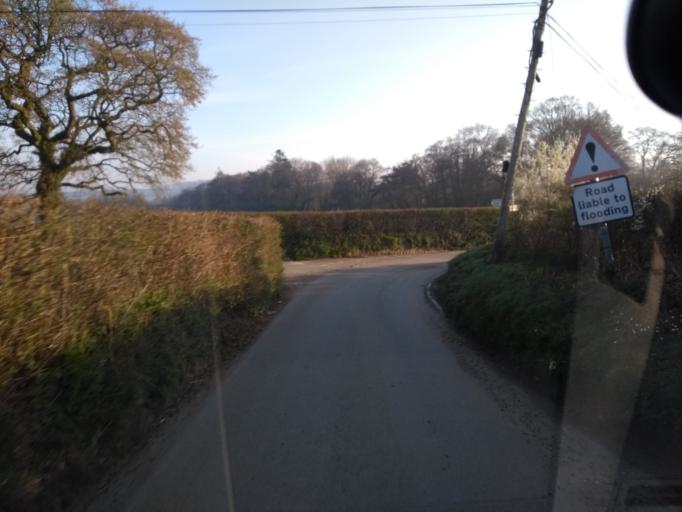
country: GB
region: England
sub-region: Somerset
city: Crewkerne
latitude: 50.8343
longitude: -2.7855
